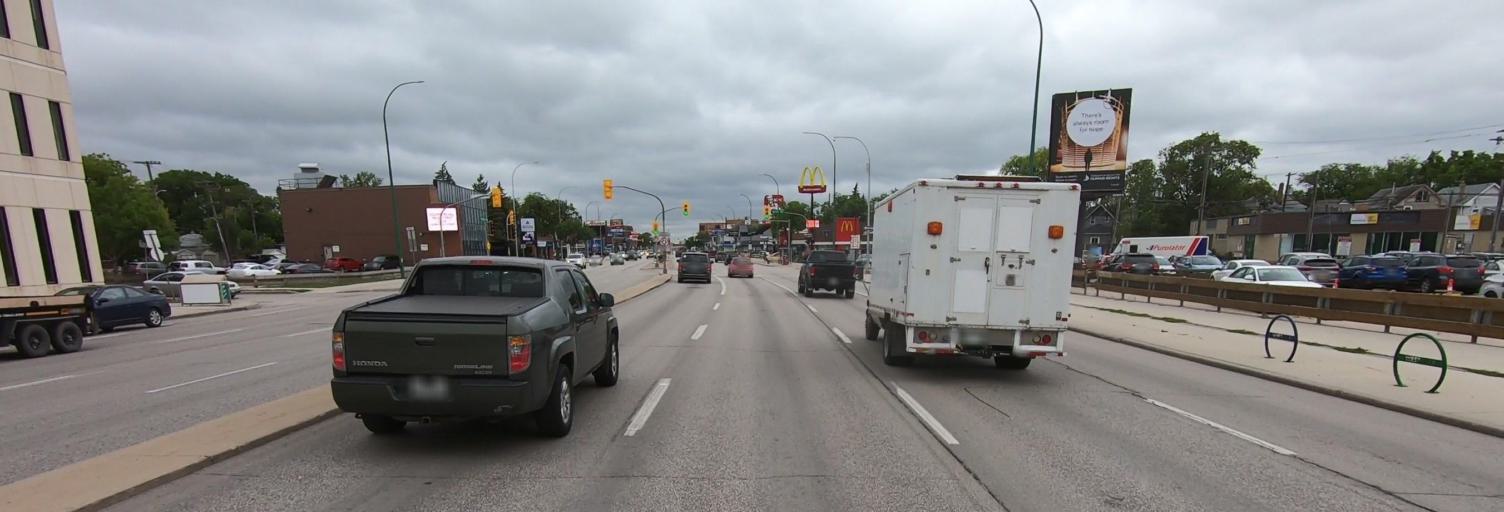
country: CA
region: Manitoba
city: Winnipeg
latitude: 49.8835
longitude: -97.1841
